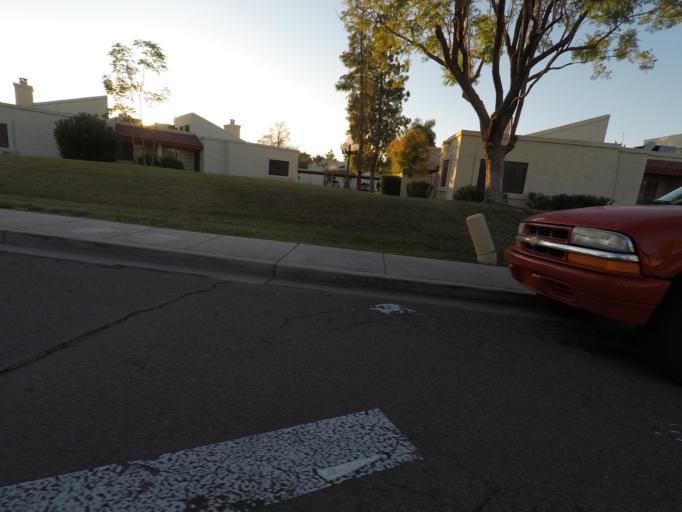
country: US
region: Arizona
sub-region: Maricopa County
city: Tempe Junction
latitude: 33.3904
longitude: -111.9479
